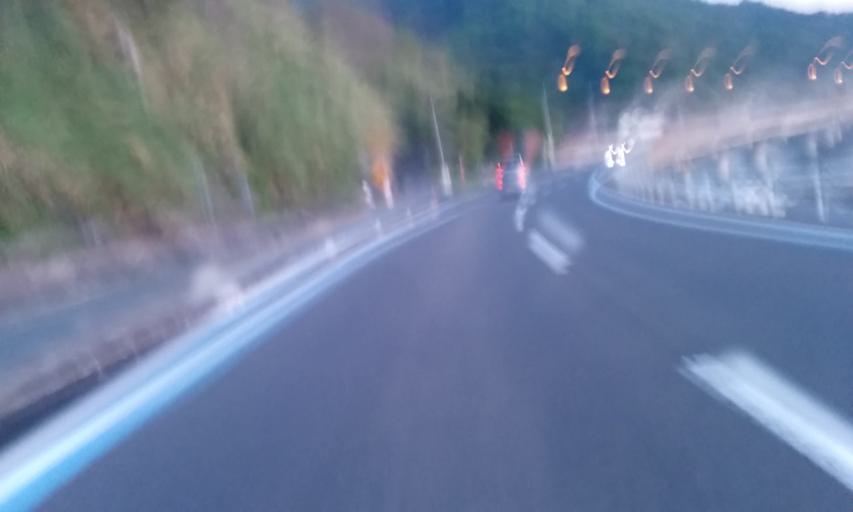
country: JP
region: Ehime
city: Ozu
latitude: 33.5915
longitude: 132.4580
